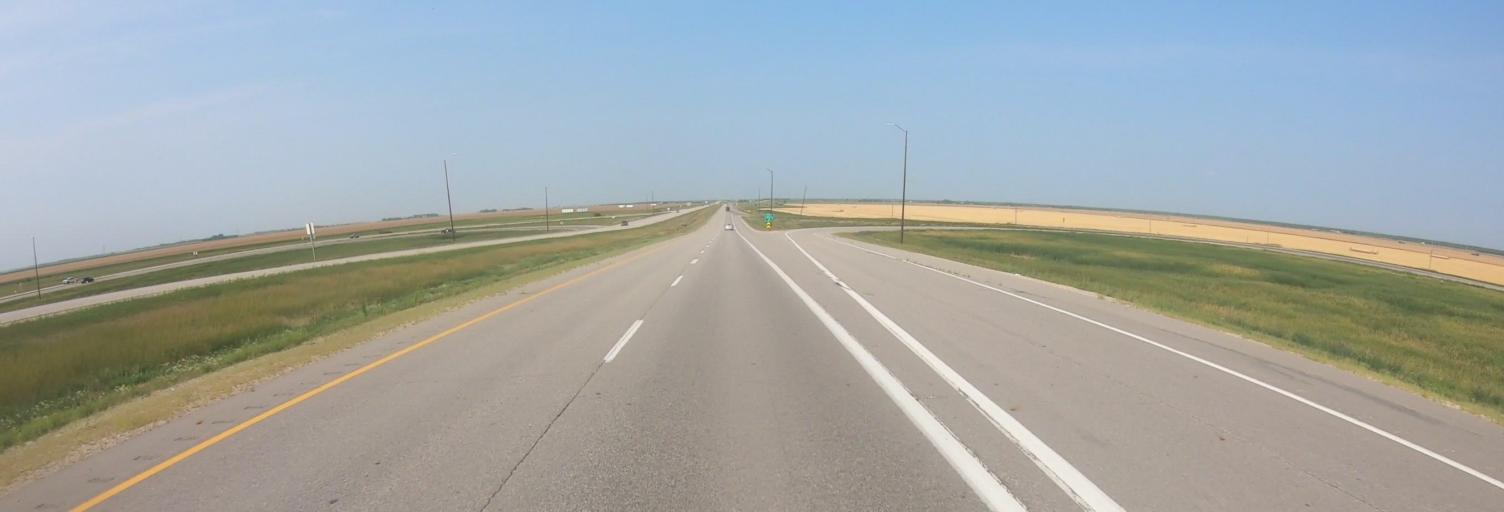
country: CA
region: Manitoba
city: Steinbach
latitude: 49.6792
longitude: -96.6610
